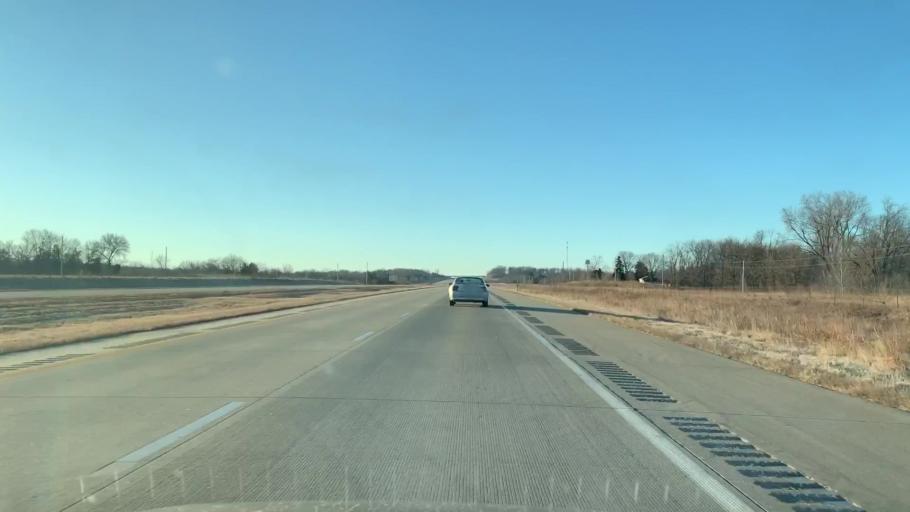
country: US
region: Kansas
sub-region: Linn County
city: Pleasanton
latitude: 38.1283
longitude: -94.7138
